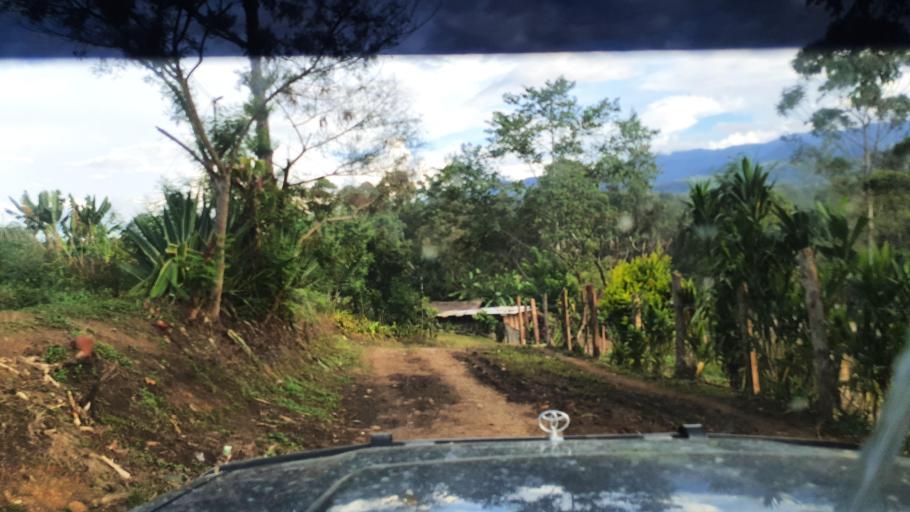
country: PG
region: Jiwaka
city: Minj
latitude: -5.9427
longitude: 144.8206
